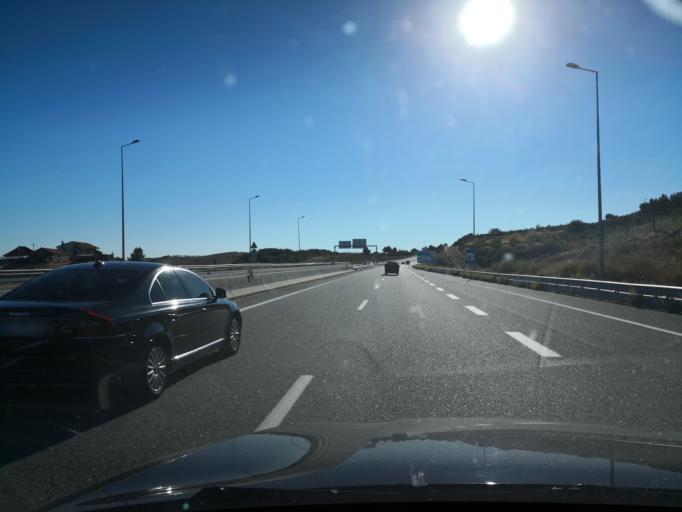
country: PT
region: Braganca
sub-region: Mirandela
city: Mirandela
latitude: 41.4487
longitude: -7.2913
